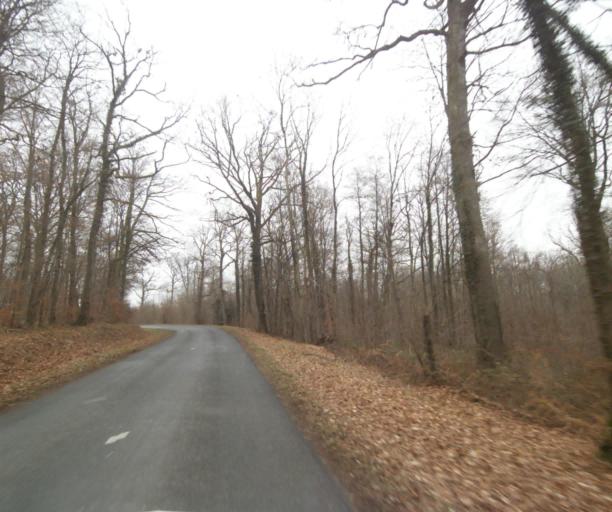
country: FR
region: Champagne-Ardenne
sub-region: Departement de la Haute-Marne
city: Bienville
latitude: 48.5645
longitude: 5.0131
